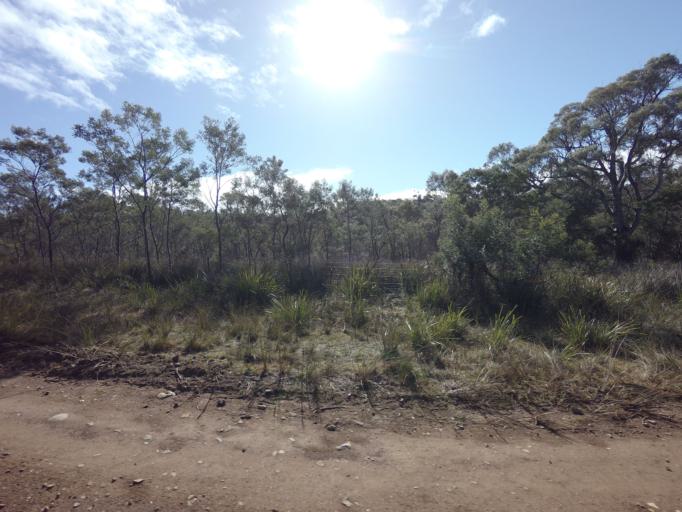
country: AU
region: Tasmania
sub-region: Sorell
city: Sorell
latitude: -42.4054
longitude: 147.9640
